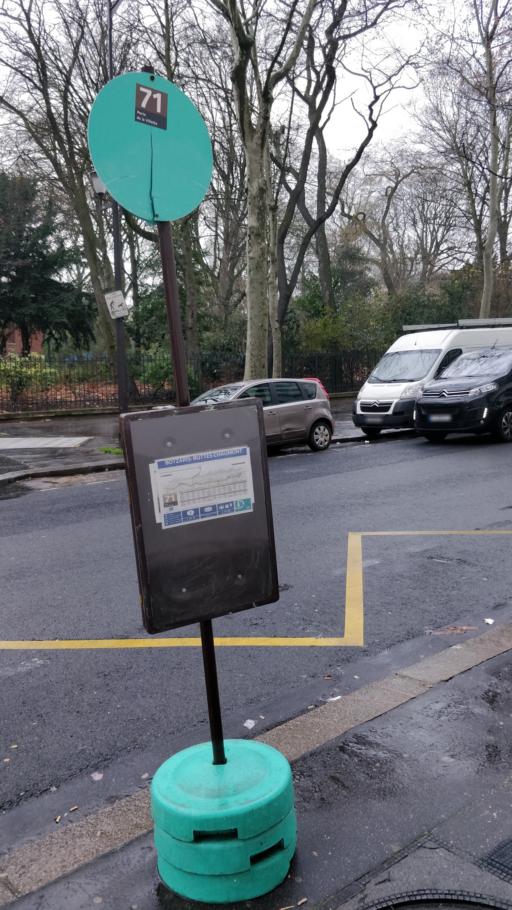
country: FR
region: Ile-de-France
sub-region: Departement de Seine-Saint-Denis
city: Le Pre-Saint-Gervais
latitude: 48.8765
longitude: 2.3814
